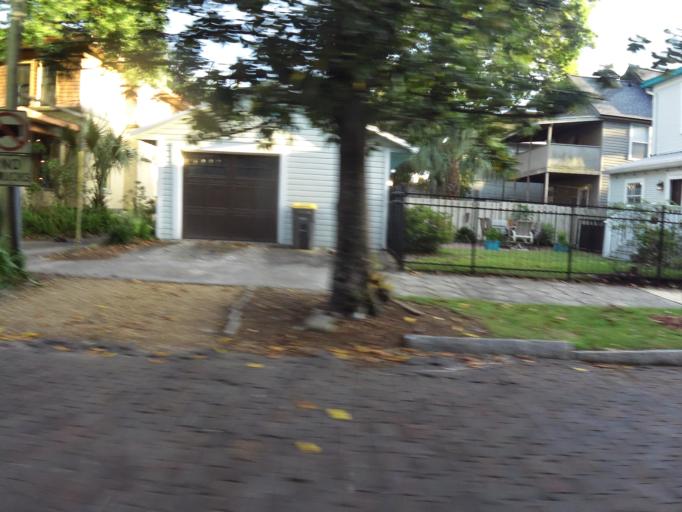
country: US
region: Florida
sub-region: Duval County
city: Jacksonville
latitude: 30.3408
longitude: -81.6588
